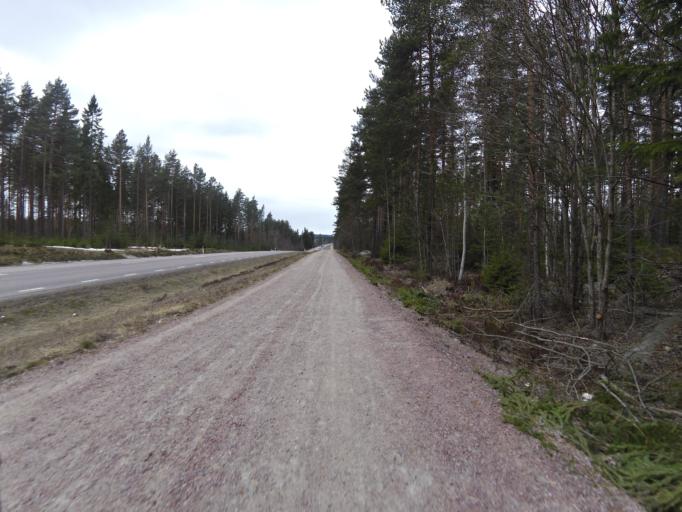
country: SE
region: Gaevleborg
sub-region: Hofors Kommun
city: Hofors
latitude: 60.5419
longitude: 16.2566
